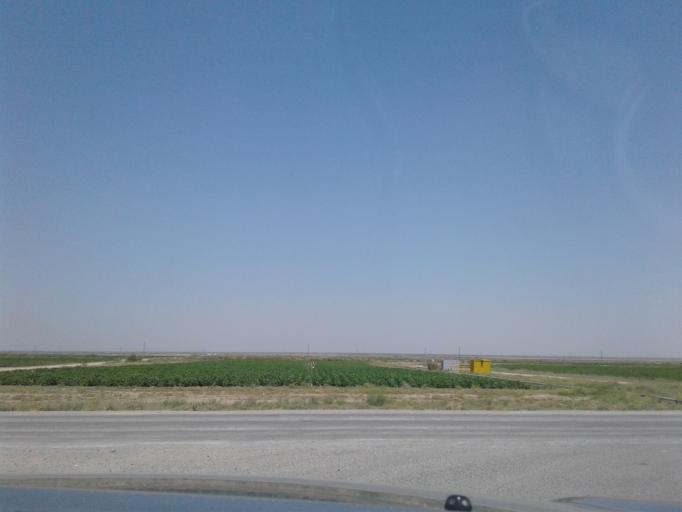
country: IR
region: Razavi Khorasan
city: Dargaz
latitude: 37.6516
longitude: 59.1509
